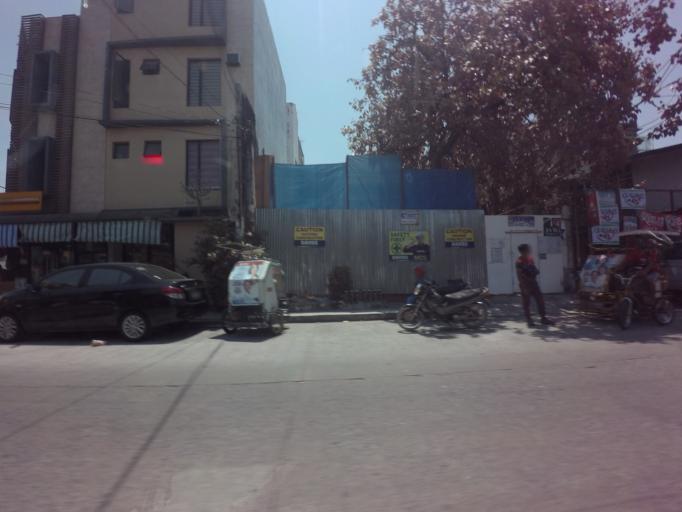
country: PH
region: Metro Manila
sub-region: Makati City
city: Makati City
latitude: 14.5595
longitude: 121.0012
